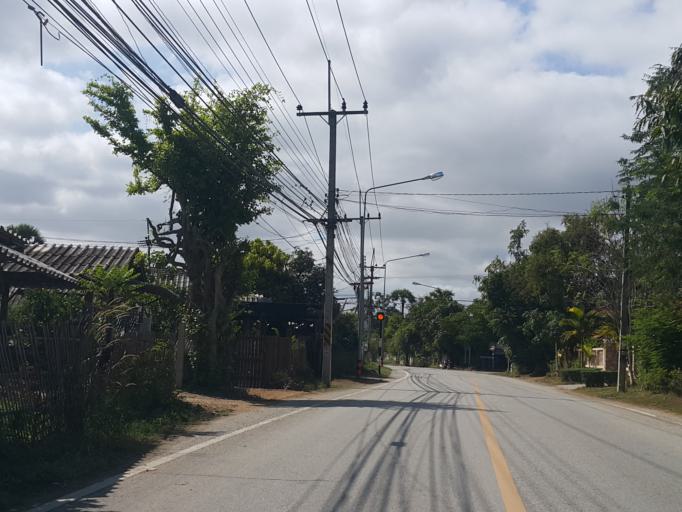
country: TH
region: Lamphun
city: Ban Thi
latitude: 18.6742
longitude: 99.1445
